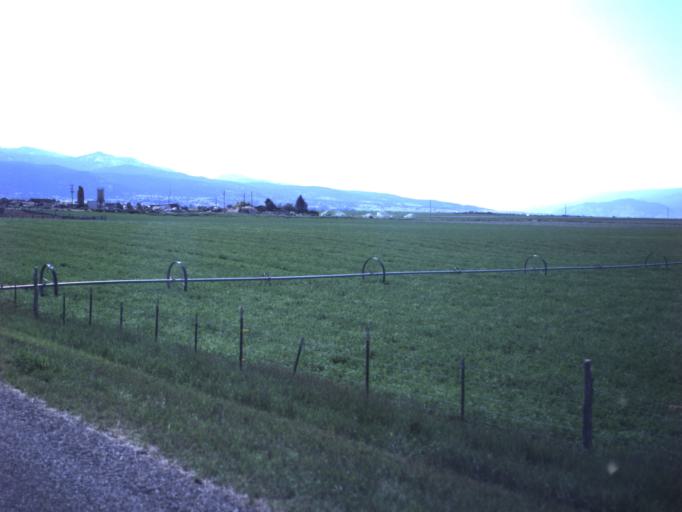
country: US
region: Utah
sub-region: Wayne County
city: Loa
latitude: 38.4116
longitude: -111.6243
